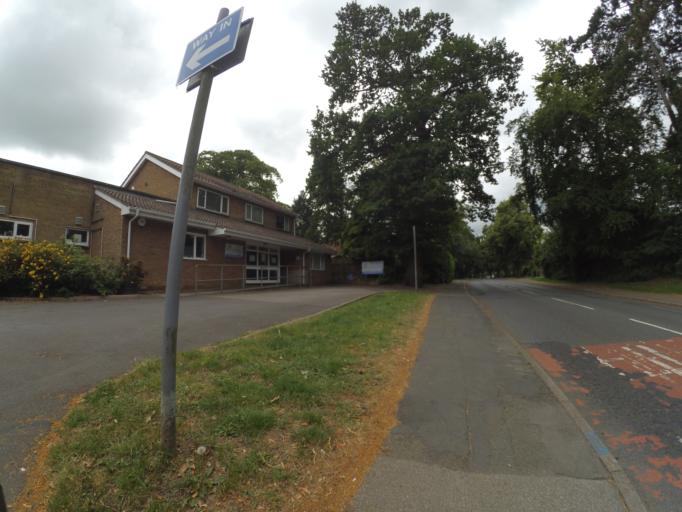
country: GB
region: England
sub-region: Warwickshire
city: Rugby
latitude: 52.3630
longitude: -1.2870
